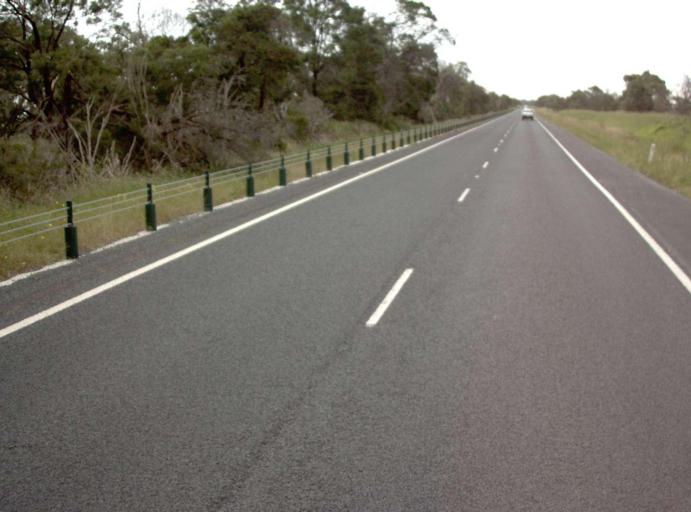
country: AU
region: Victoria
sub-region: Casey
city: Blind Bight
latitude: -38.1797
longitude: 145.3385
